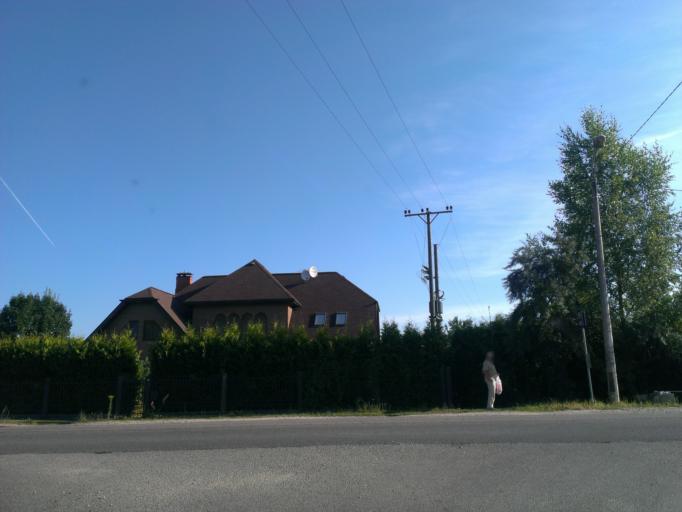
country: LV
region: Riga
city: Bergi
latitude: 56.9874
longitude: 24.3038
